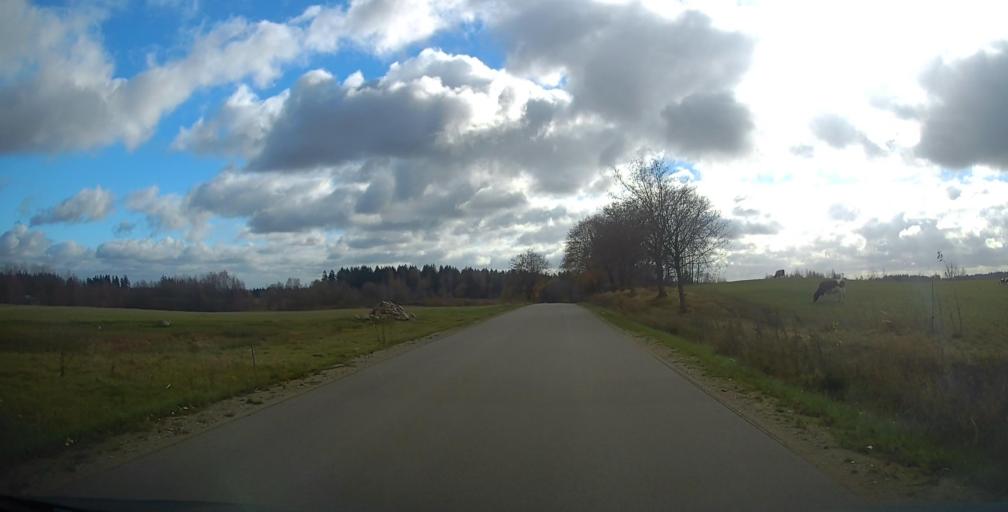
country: PL
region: Podlasie
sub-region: Suwalki
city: Suwalki
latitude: 54.3146
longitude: 22.8775
